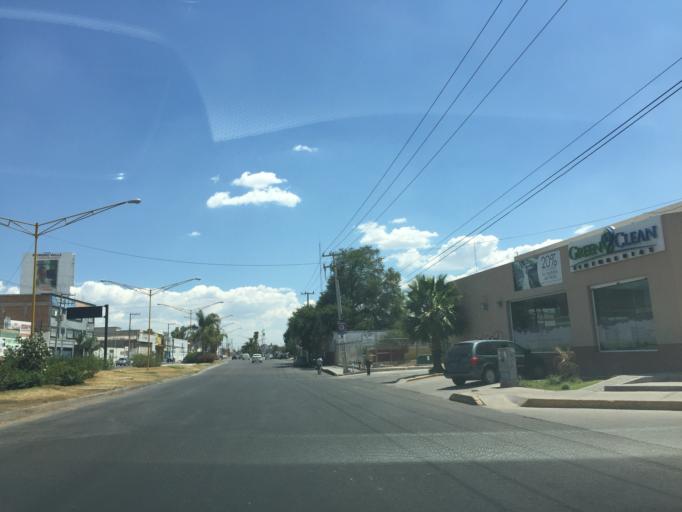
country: MX
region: Aguascalientes
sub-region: Aguascalientes
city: La Loma de los Negritos
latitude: 21.8579
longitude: -102.3148
